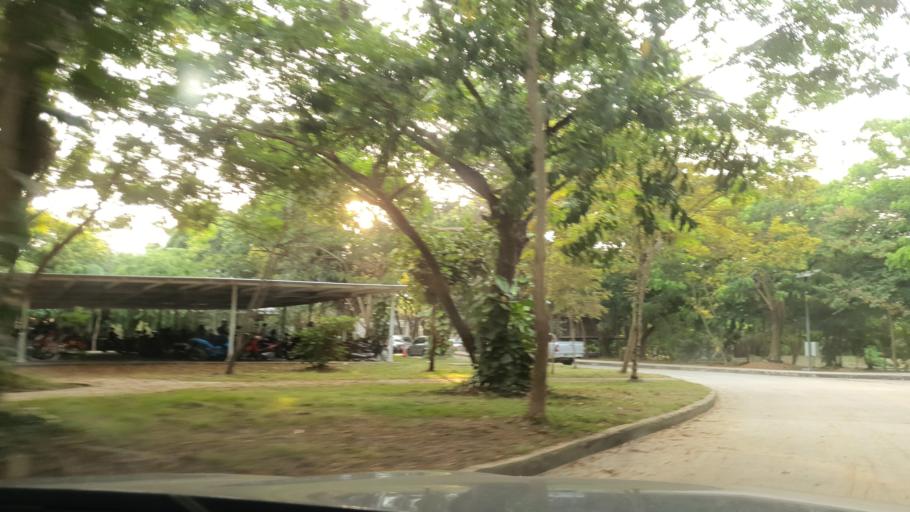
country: TH
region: Chiang Mai
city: Saraphi
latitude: 18.7450
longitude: 99.0381
